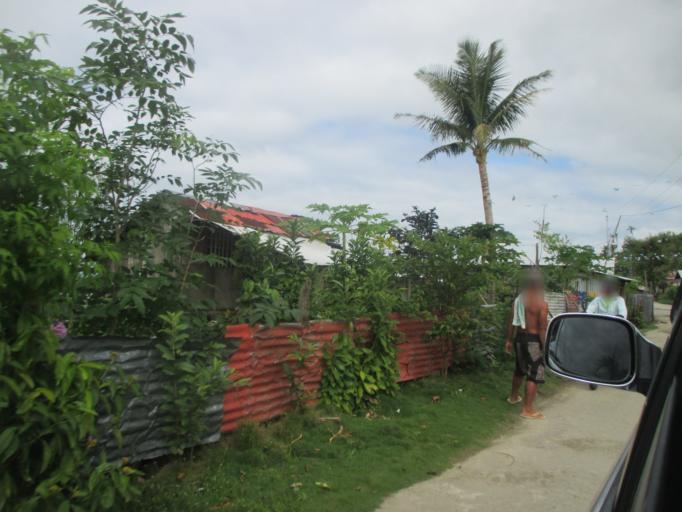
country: PH
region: Eastern Visayas
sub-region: Province of Eastern Samar
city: Lawa-an
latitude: 11.1096
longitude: 125.2118
